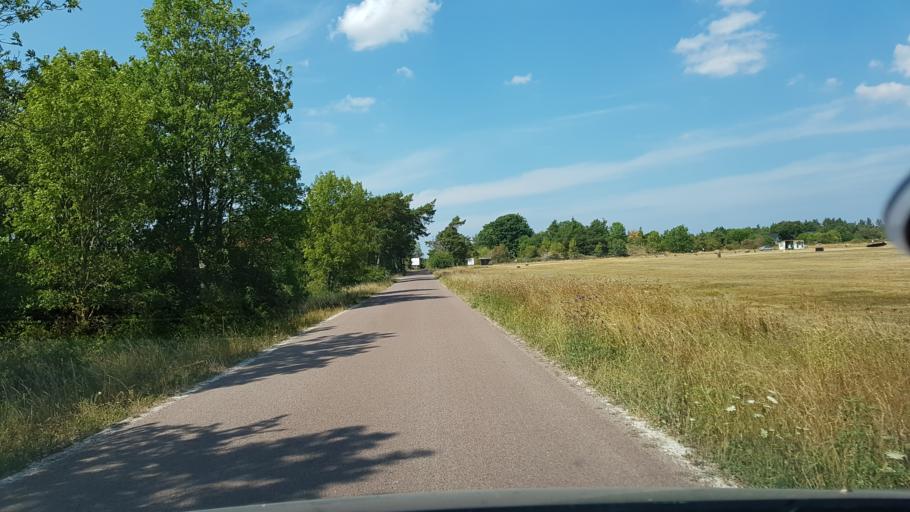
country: SE
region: Gotland
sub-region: Gotland
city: Visby
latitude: 57.6675
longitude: 18.3685
